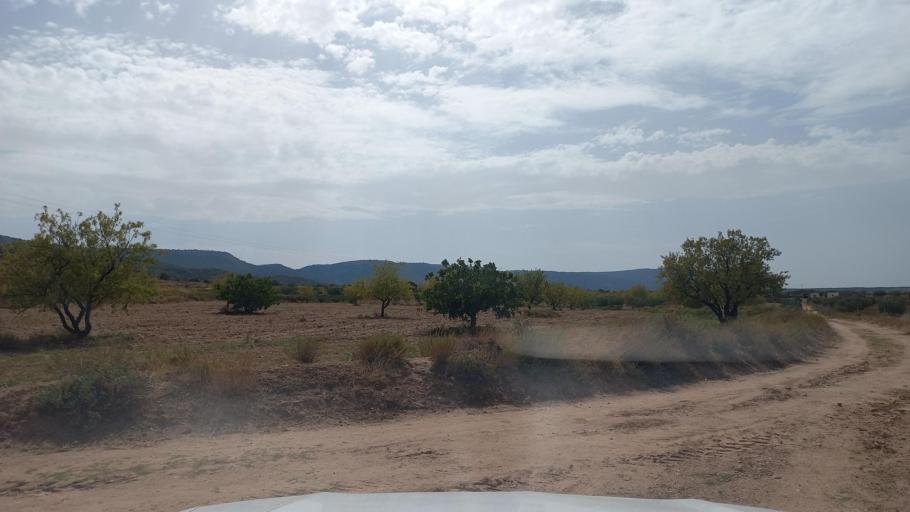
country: TN
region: Al Qasrayn
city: Kasserine
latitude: 35.3537
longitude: 8.8754
